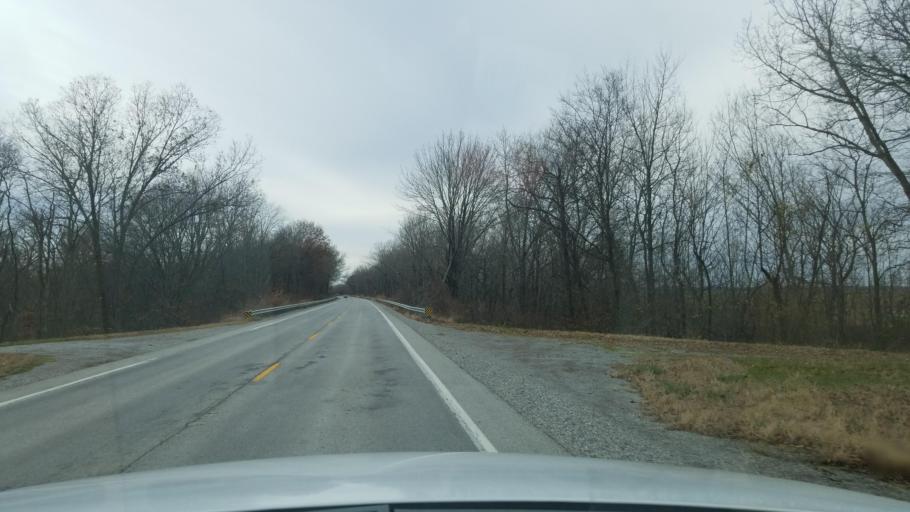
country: US
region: Indiana
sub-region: Posey County
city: Mount Vernon
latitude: 37.9417
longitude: -88.0616
